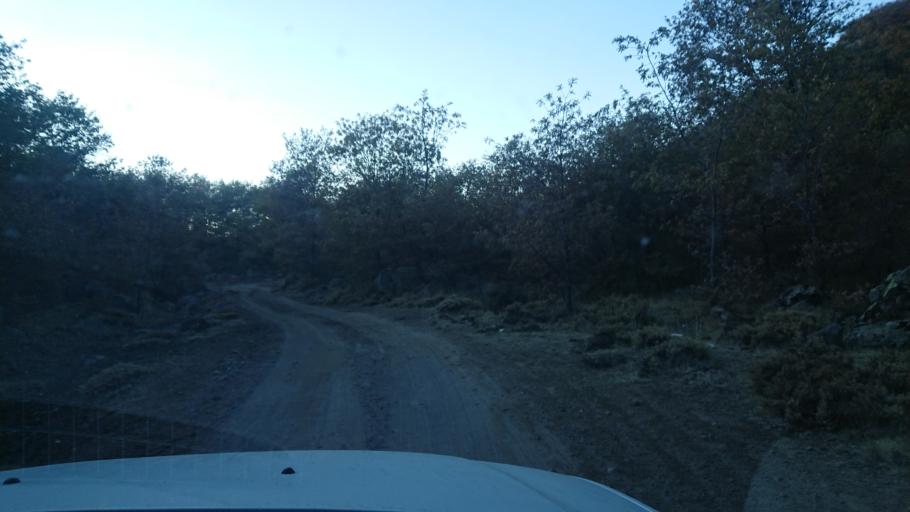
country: TR
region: Aksaray
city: Taspinar
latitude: 38.1647
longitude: 34.2094
